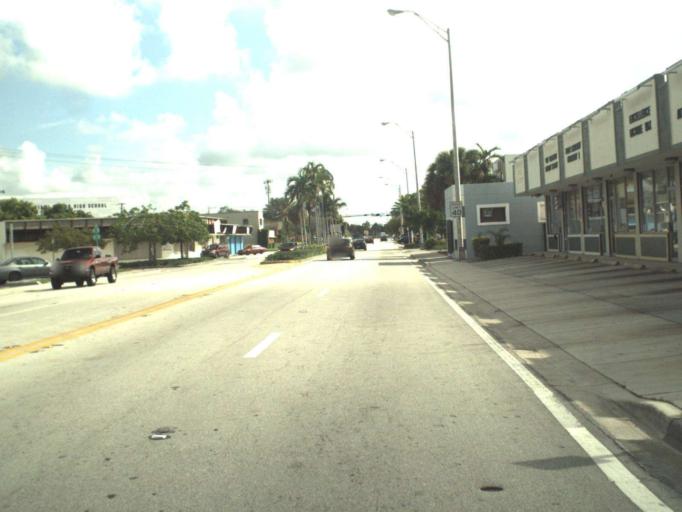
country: US
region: Florida
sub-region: Miami-Dade County
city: North Miami
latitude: 25.8933
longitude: -80.1841
